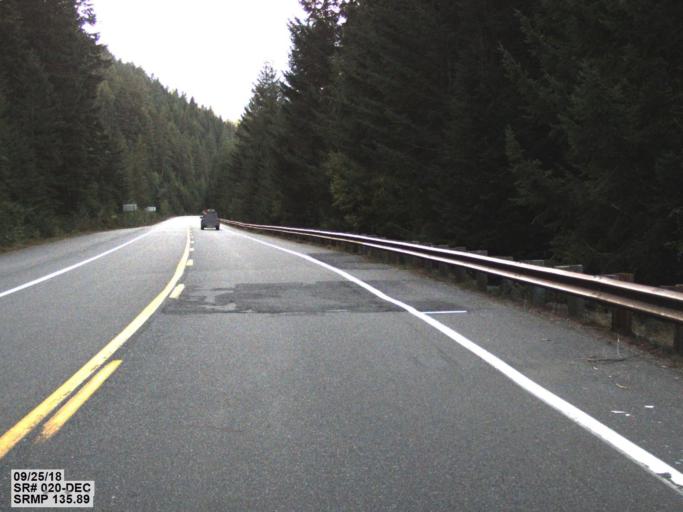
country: US
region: Washington
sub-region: Snohomish County
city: Darrington
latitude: 48.7242
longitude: -121.0249
